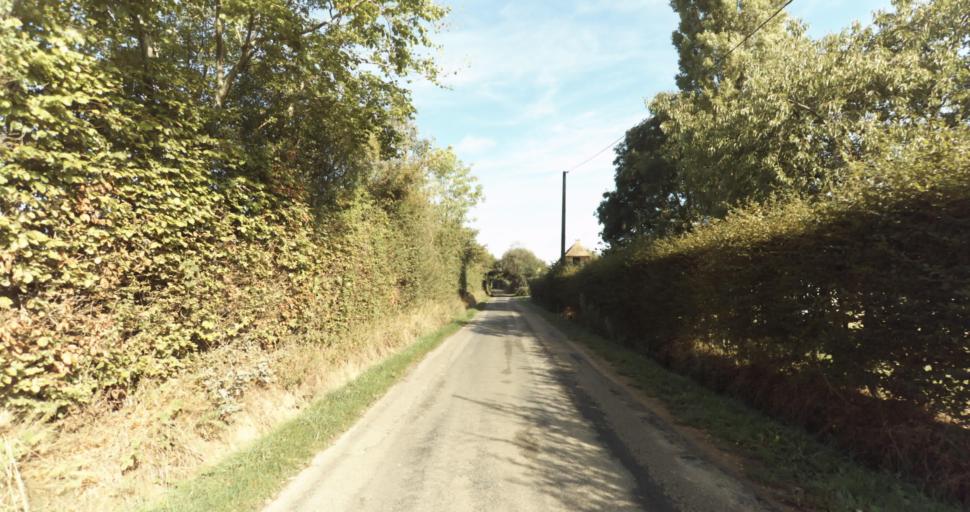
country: FR
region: Lower Normandy
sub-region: Departement de l'Orne
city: Vimoutiers
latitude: 48.9195
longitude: 0.2980
